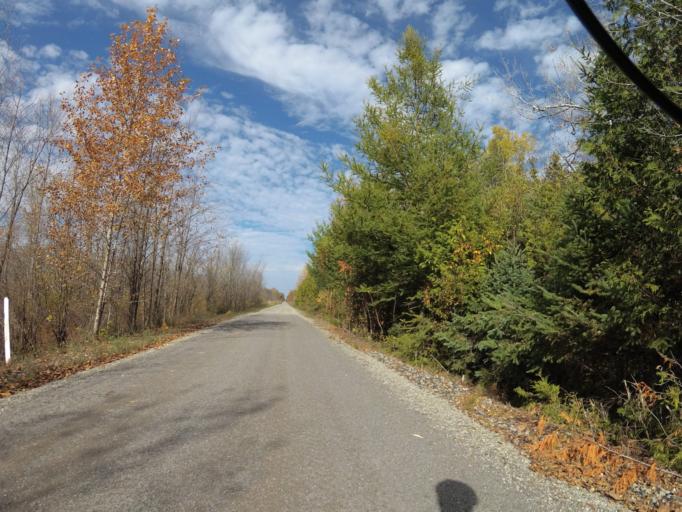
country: CA
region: Ontario
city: Carleton Place
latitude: 45.0553
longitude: -76.0914
